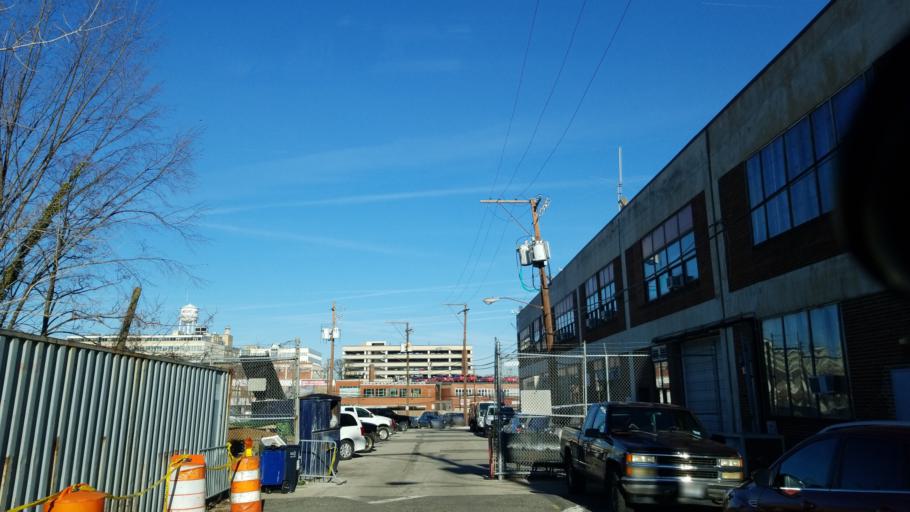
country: US
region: Maryland
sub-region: Prince George's County
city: Mount Rainier
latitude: 38.9127
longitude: -76.9813
